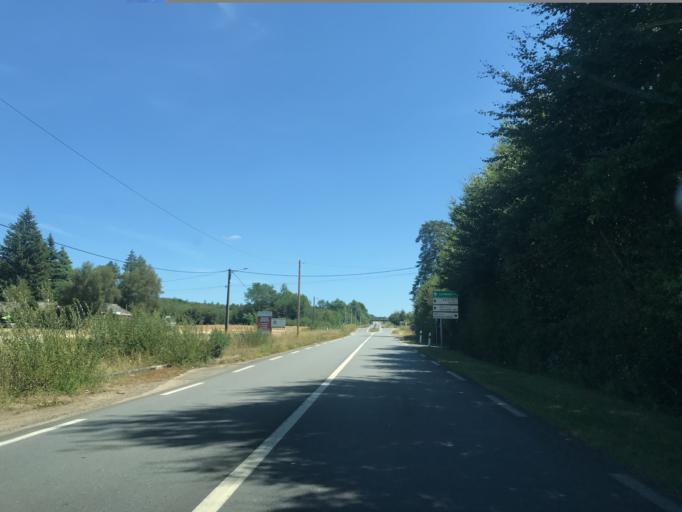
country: FR
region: Limousin
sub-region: Departement de la Correze
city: Correze
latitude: 45.3333
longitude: 1.8877
